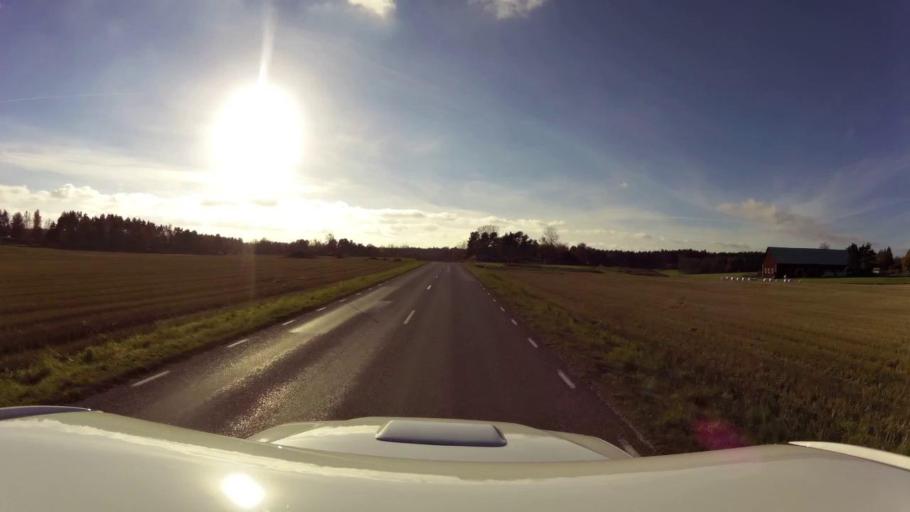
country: SE
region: OEstergoetland
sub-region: Linkopings Kommun
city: Vikingstad
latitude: 58.3049
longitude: 15.4840
